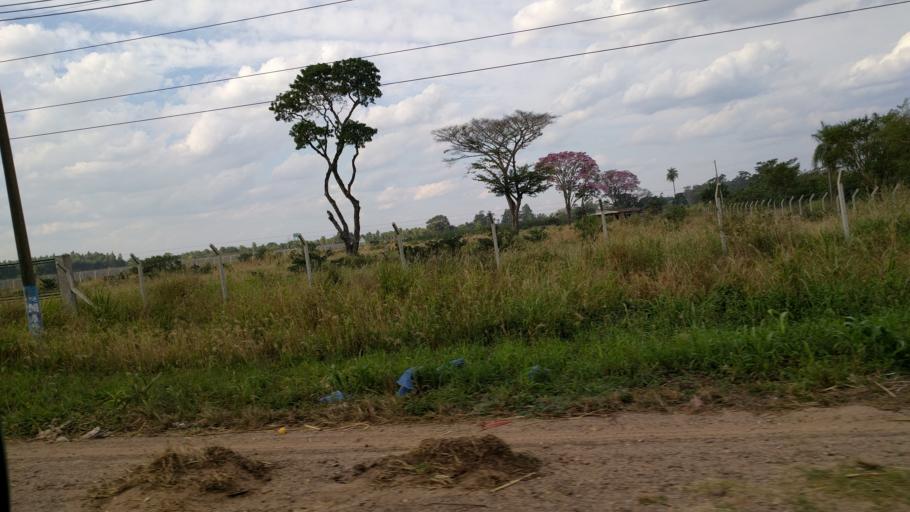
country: BO
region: Santa Cruz
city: La Belgica
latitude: -17.5638
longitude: -63.1590
